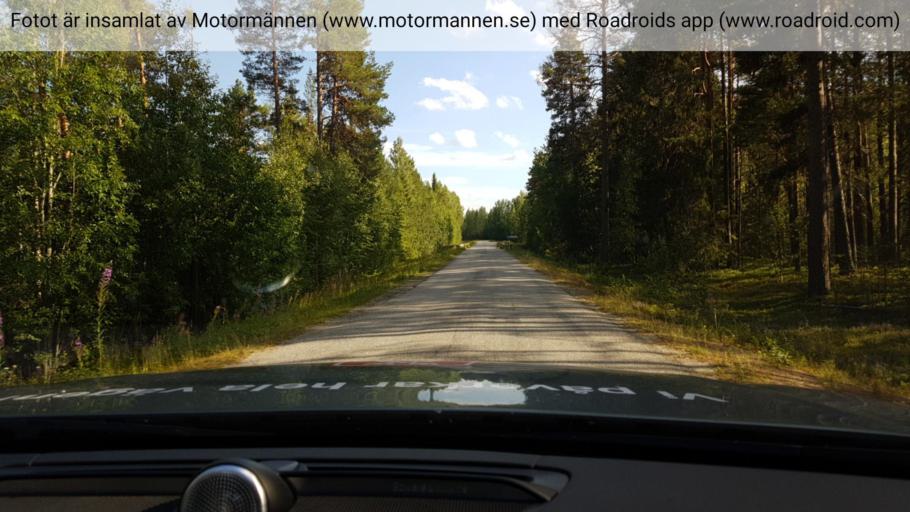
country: SE
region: Vaesterbotten
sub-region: Dorotea Kommun
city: Dorotea
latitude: 63.9169
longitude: 16.2653
